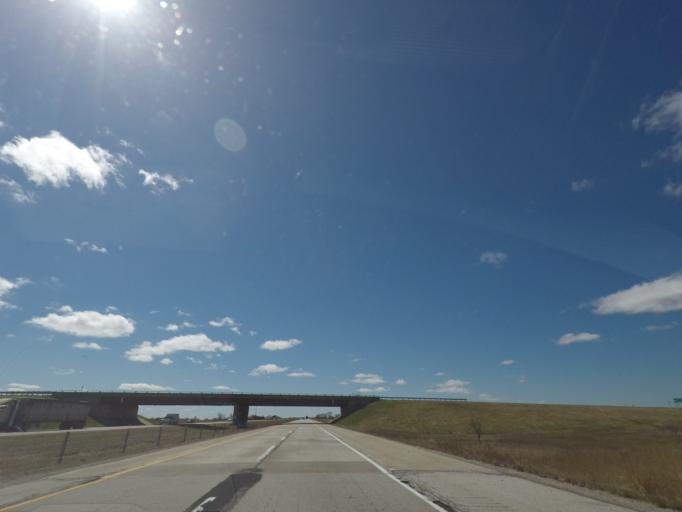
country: US
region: Illinois
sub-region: Livingston County
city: Odell
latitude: 41.0068
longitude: -88.5366
